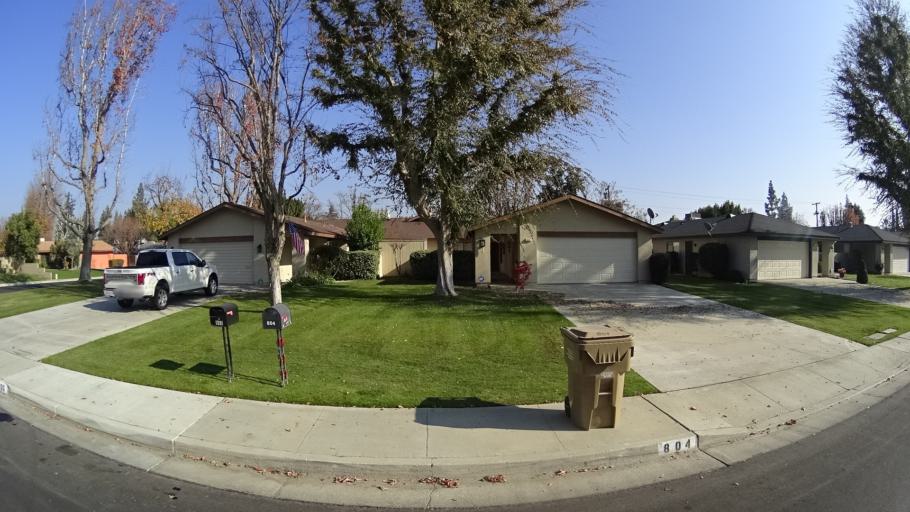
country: US
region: California
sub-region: Kern County
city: Bakersfield
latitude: 35.3475
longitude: -119.0624
